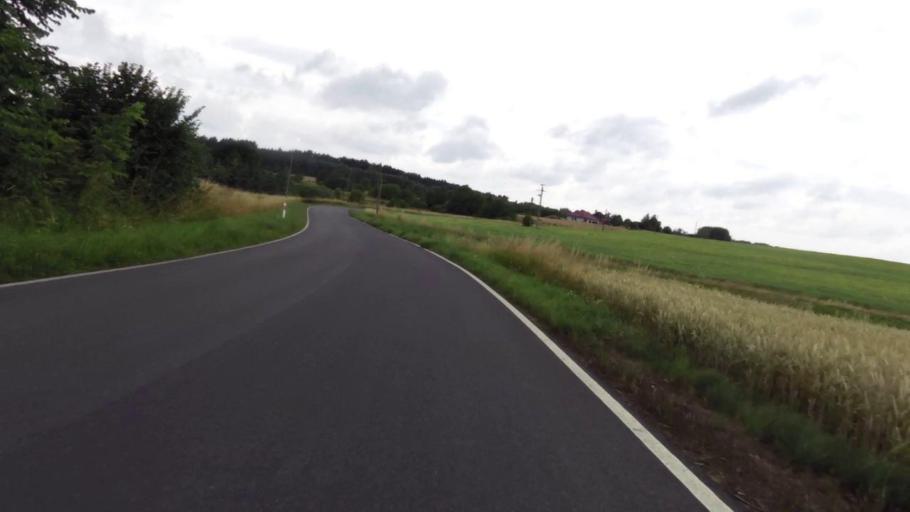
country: PL
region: West Pomeranian Voivodeship
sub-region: Powiat mysliborski
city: Mysliborz
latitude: 52.9402
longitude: 14.8734
